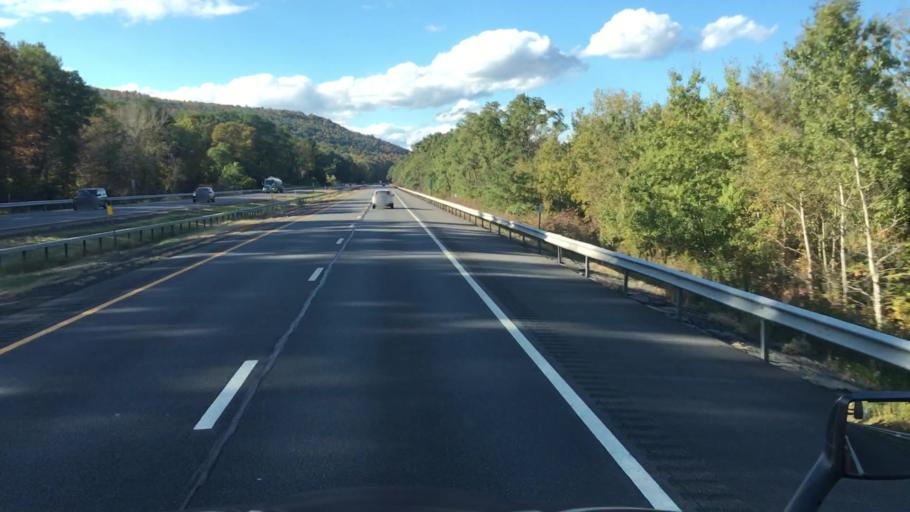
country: US
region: New York
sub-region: Schenectady County
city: Scotia
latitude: 42.8463
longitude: -74.0214
